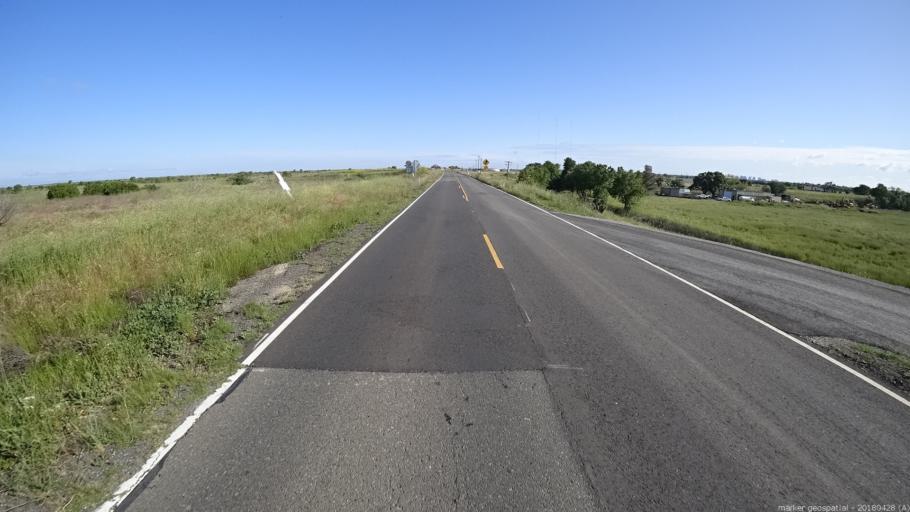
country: US
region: California
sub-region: Yolo County
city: West Sacramento
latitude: 38.5027
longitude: -121.5820
